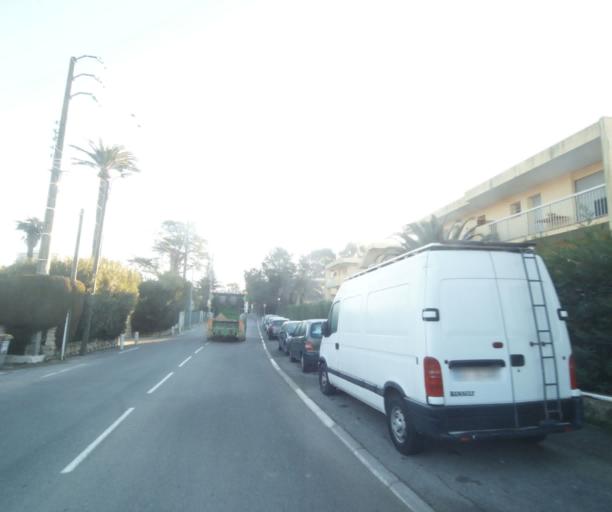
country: FR
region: Provence-Alpes-Cote d'Azur
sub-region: Departement des Alpes-Maritimes
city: Vallauris
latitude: 43.5753
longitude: 7.0849
